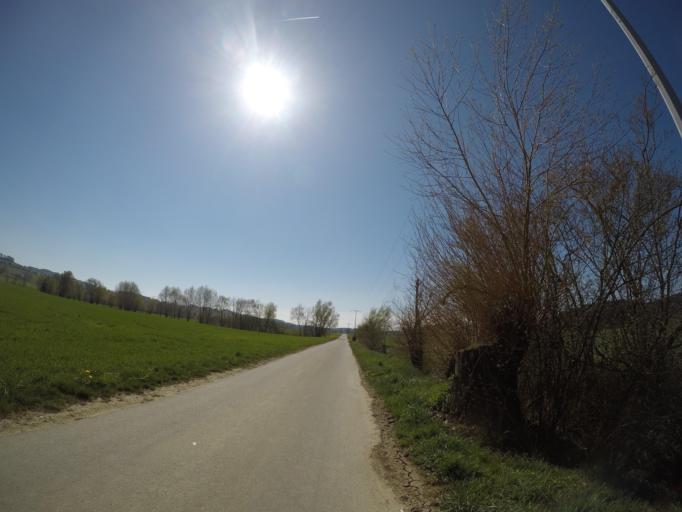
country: DE
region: Baden-Wuerttemberg
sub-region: Tuebingen Region
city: Wilhelmsdorf
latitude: 47.8392
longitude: 9.4446
